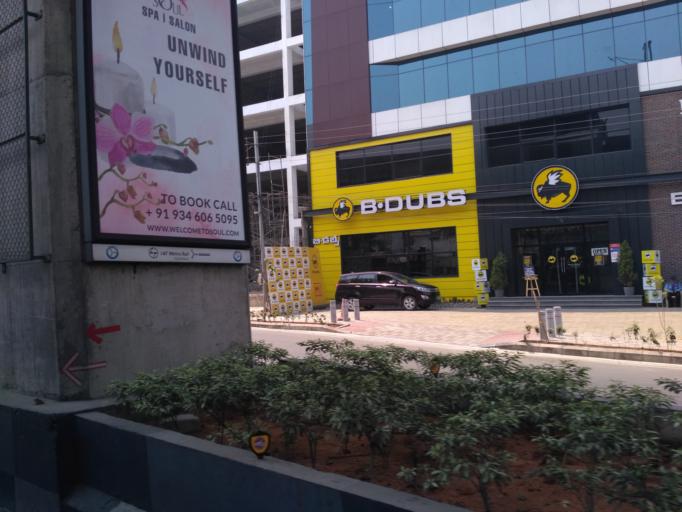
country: IN
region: Telangana
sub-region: Rangareddi
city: Kukatpalli
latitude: 17.4338
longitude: 78.4052
